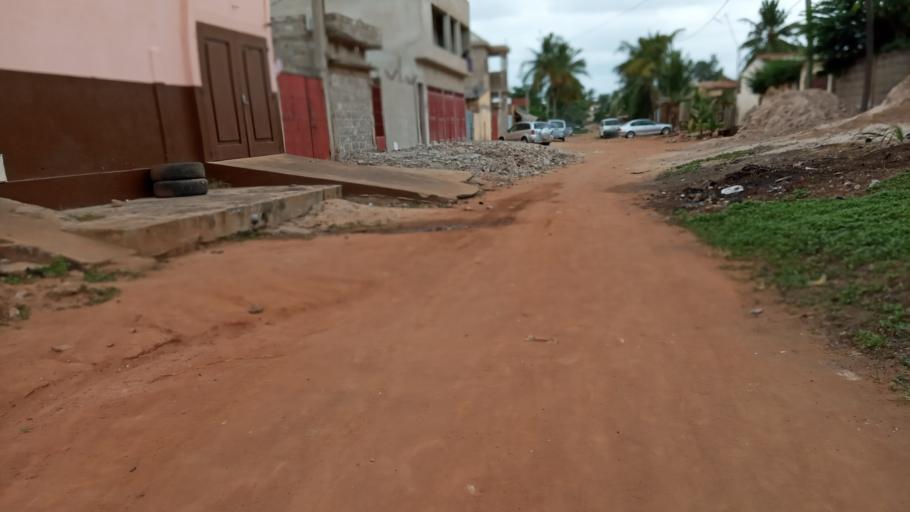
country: TG
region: Maritime
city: Lome
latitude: 6.1825
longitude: 1.1738
